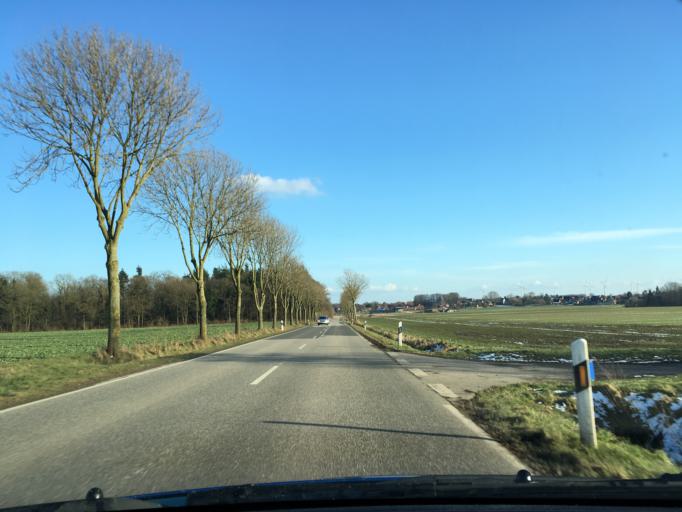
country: DE
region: Schleswig-Holstein
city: Lutau
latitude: 53.4412
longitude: 10.5290
